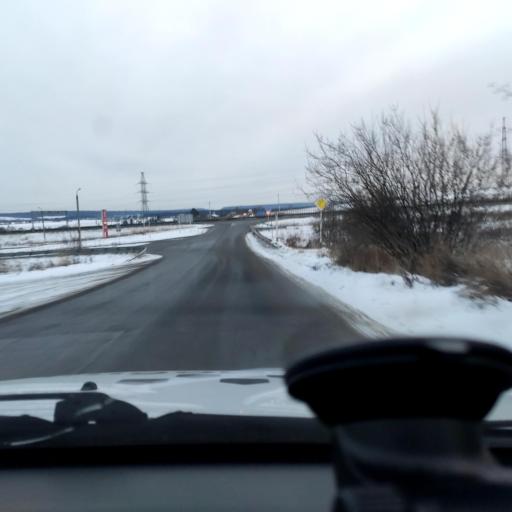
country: RU
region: Perm
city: Ferma
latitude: 57.9320
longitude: 56.3280
